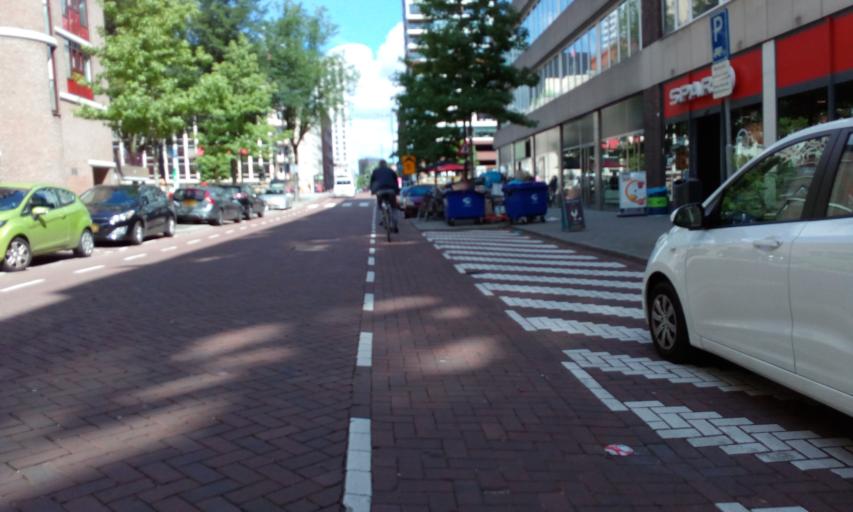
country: NL
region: South Holland
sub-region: Gemeente Rotterdam
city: Rotterdam
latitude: 51.9162
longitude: 4.4858
